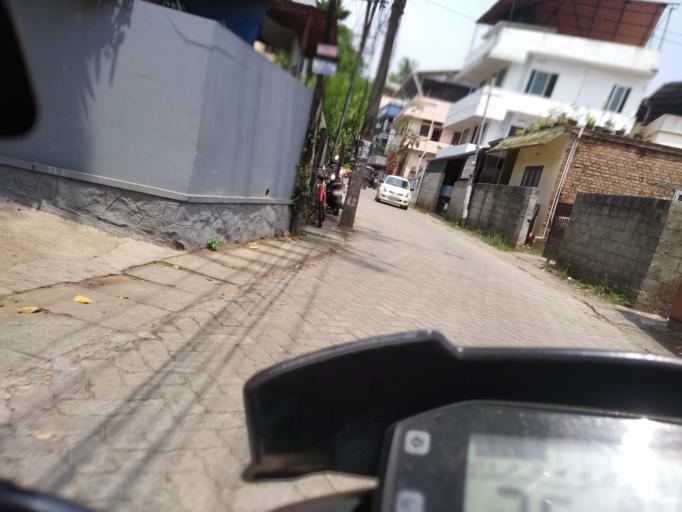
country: IN
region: Kerala
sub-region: Ernakulam
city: Elur
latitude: 10.0126
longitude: 76.3211
